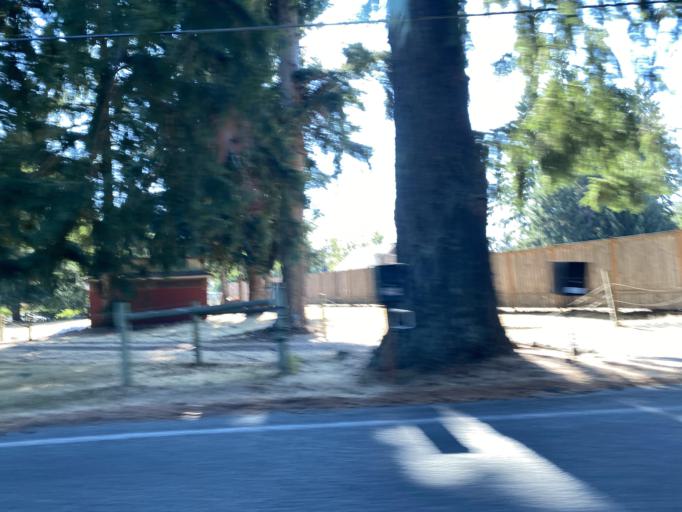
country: US
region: Washington
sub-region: Thurston County
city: Tanglewilde-Thompson Place
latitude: 46.9880
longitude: -122.7389
